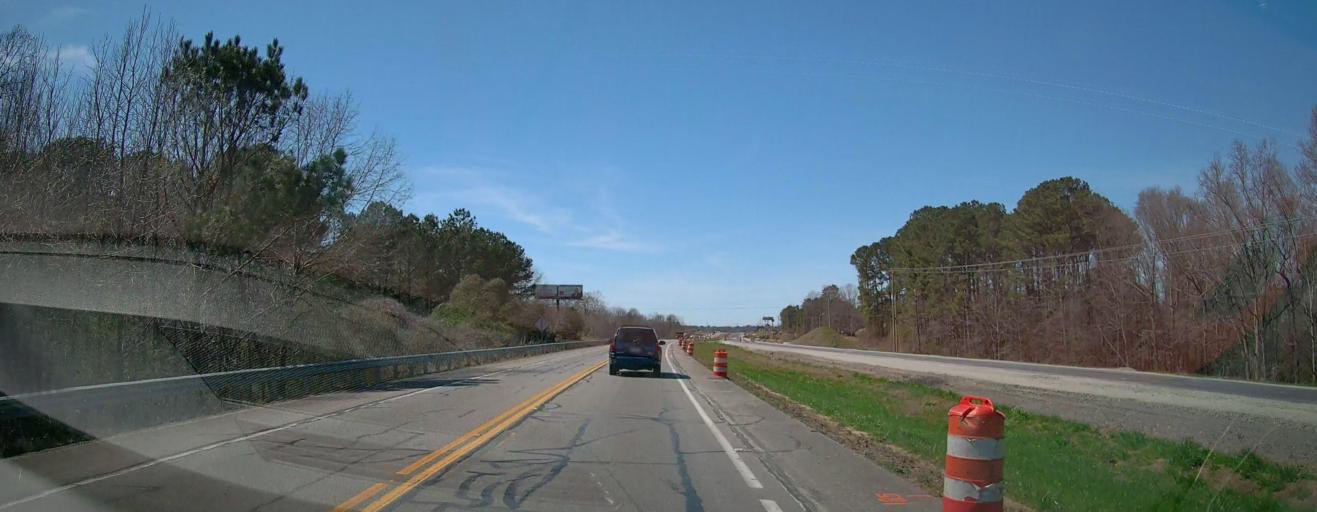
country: US
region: Alabama
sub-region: Cullman County
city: Cullman
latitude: 34.1999
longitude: -86.8183
